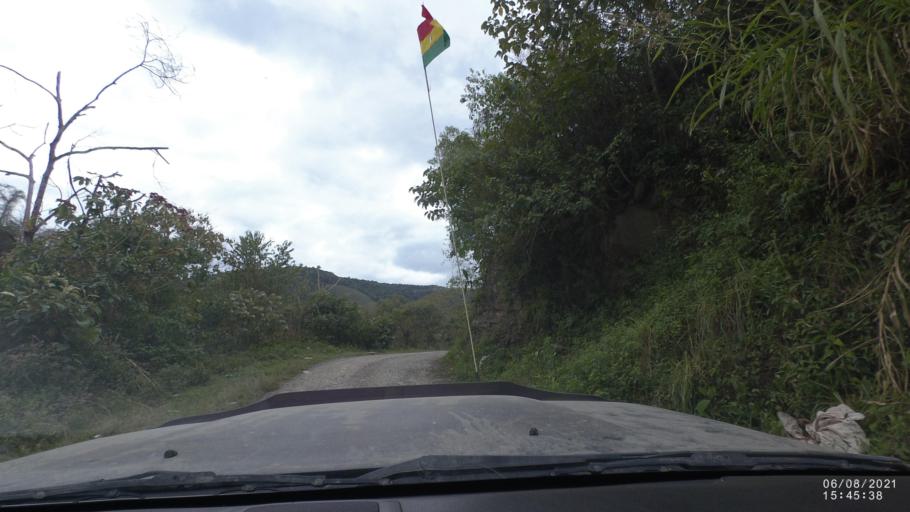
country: BO
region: La Paz
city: Quime
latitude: -16.5958
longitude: -66.7111
